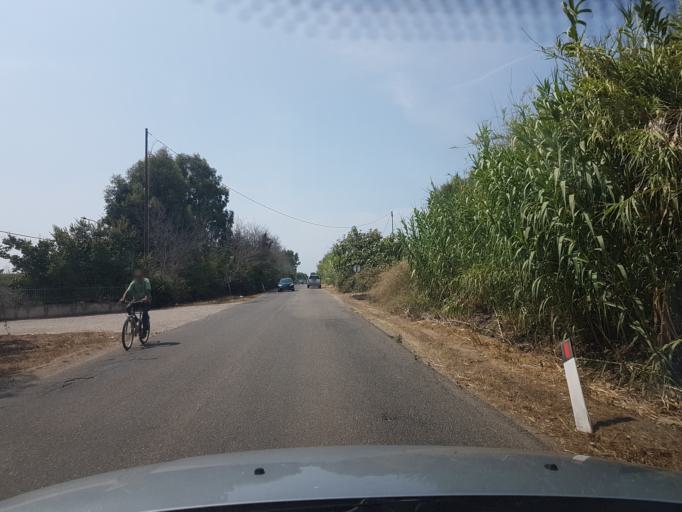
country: IT
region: Sardinia
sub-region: Provincia di Oristano
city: Solanas
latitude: 39.9214
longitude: 8.5453
